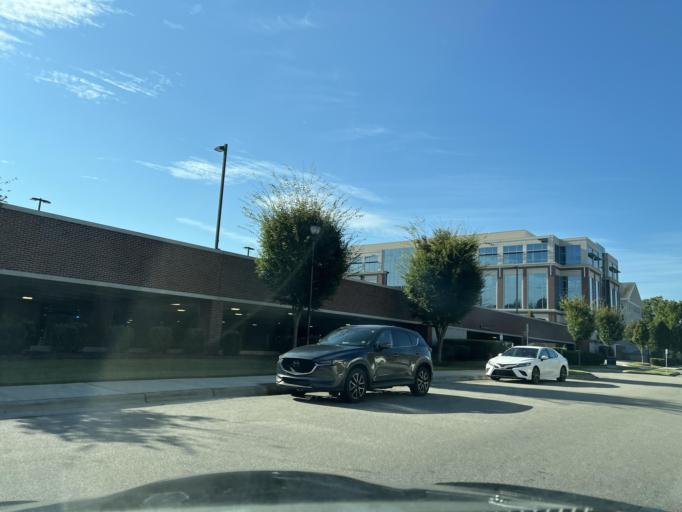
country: US
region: North Carolina
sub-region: Wake County
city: Cary
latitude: 35.8094
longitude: -78.7302
